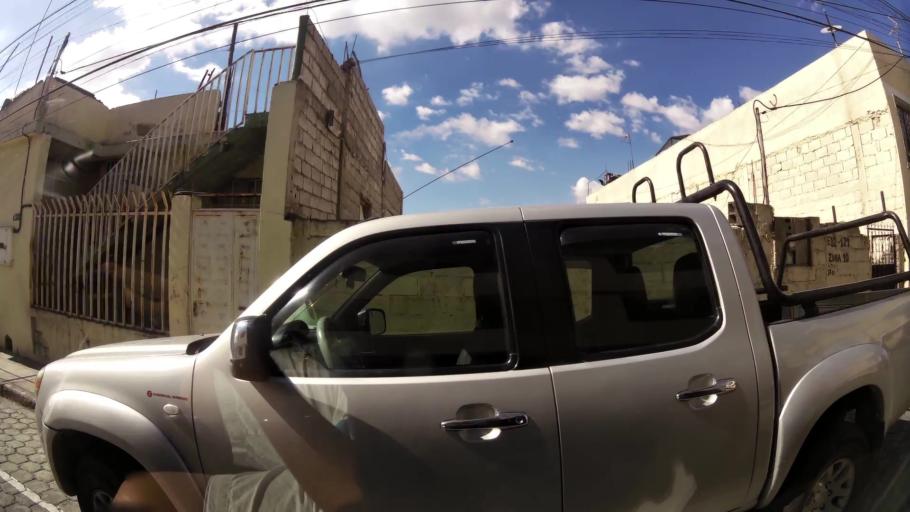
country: EC
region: Pichincha
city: Quito
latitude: -0.1185
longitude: -78.4673
